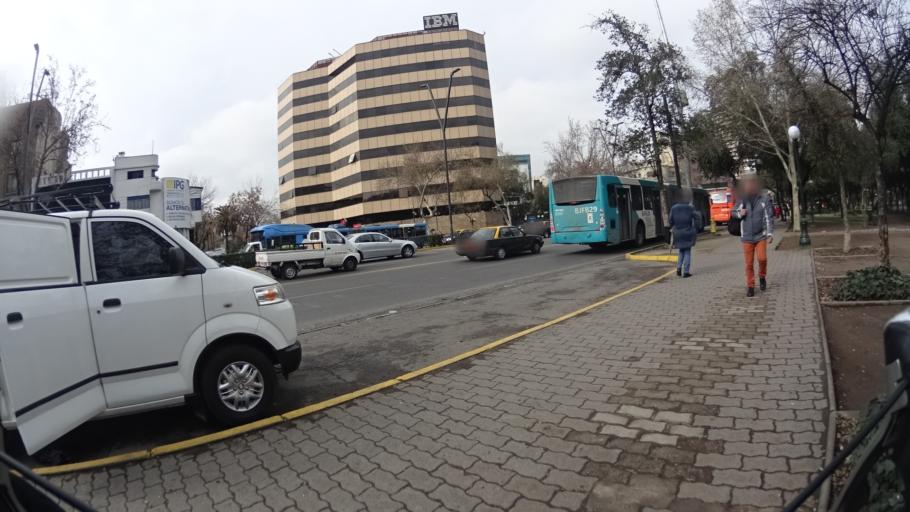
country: CL
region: Santiago Metropolitan
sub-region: Provincia de Santiago
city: Santiago
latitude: -33.4328
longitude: -70.6260
